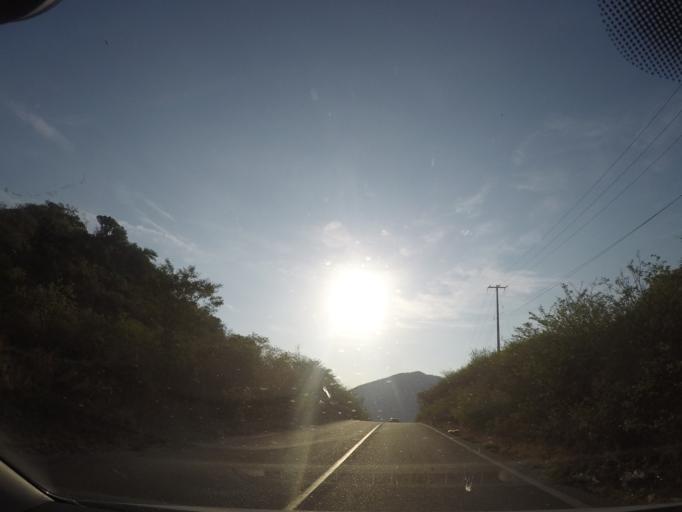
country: MX
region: Oaxaca
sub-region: Santo Domingo Tehuantepec
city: La Noria
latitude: 16.2363
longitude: -95.1650
